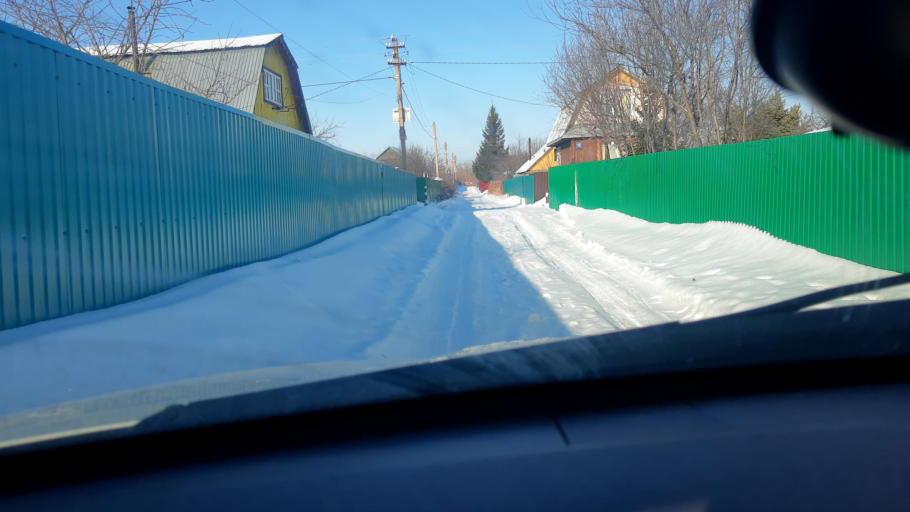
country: RU
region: Bashkortostan
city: Ufa
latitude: 54.5776
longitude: 55.8915
